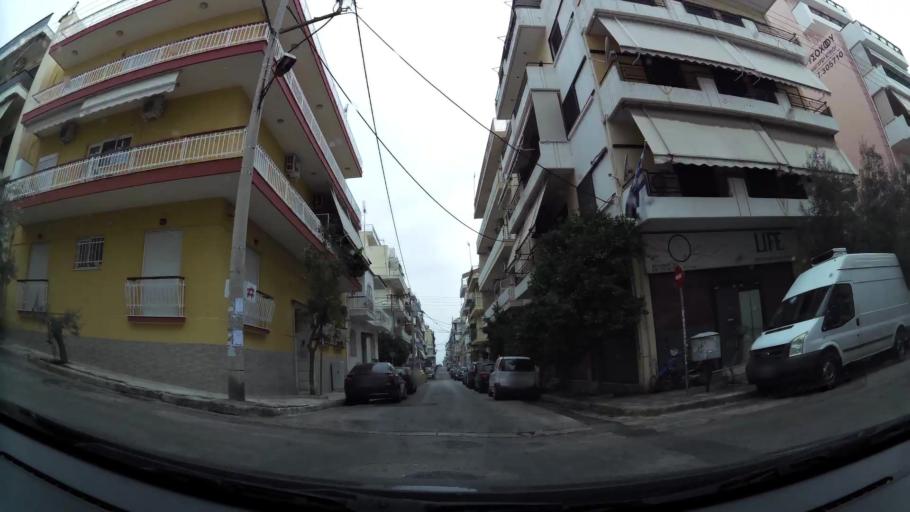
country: GR
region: Attica
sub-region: Nomos Attikis
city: Piraeus
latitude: 37.9315
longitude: 23.6360
